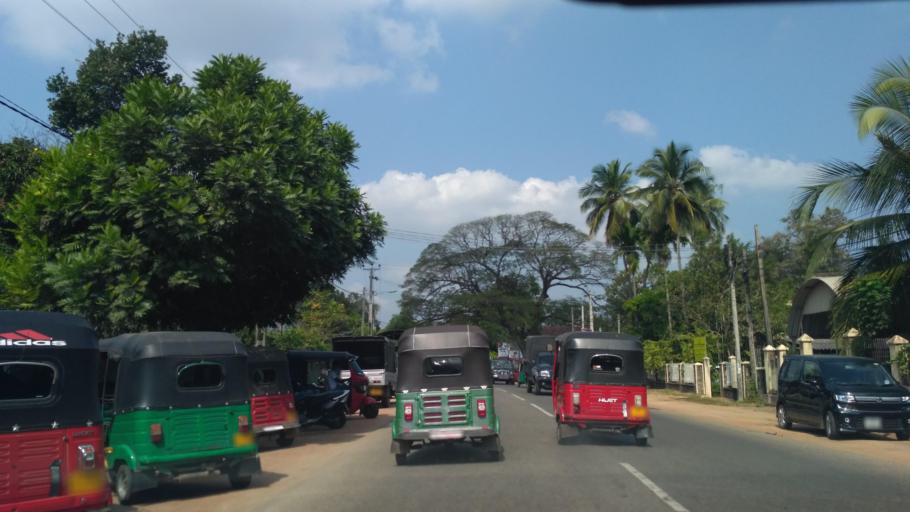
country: LK
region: North Western
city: Kurunegala
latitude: 7.4853
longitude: 80.3536
